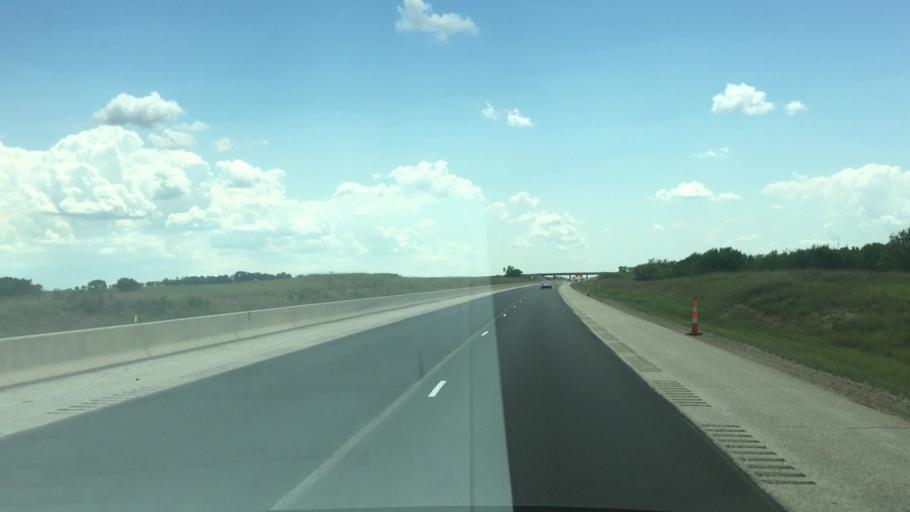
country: US
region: Kansas
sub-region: Lyon County
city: Emporia
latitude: 38.5776
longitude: -96.0918
